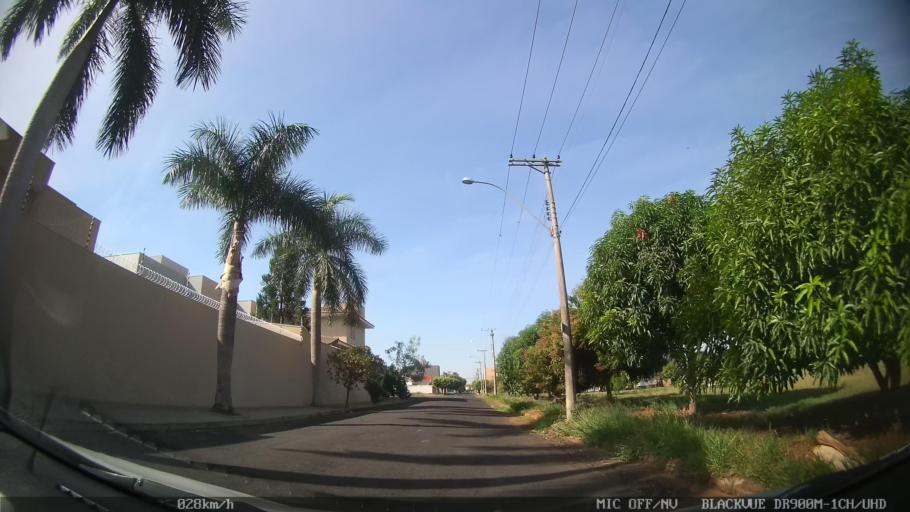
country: BR
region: Sao Paulo
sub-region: Sao Jose Do Rio Preto
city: Sao Jose do Rio Preto
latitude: -20.8017
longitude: -49.4136
